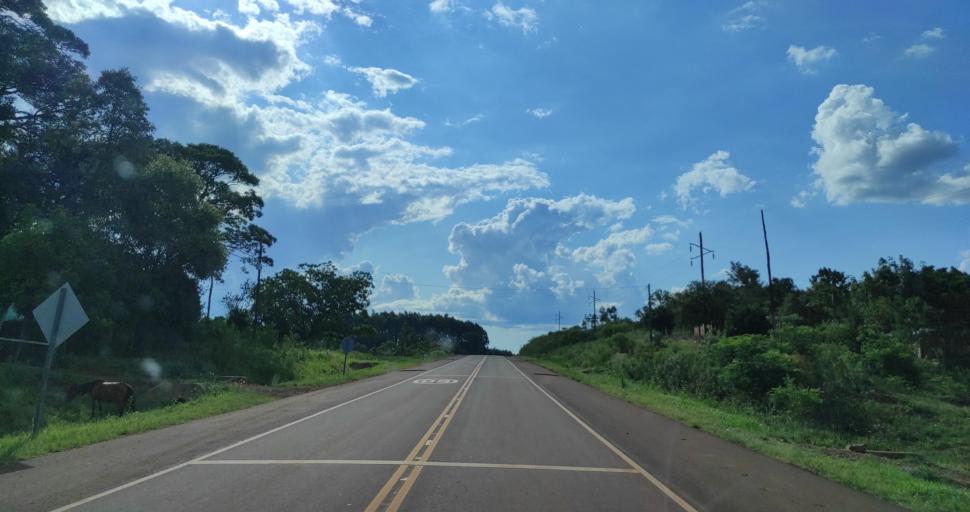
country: AR
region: Misiones
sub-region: Departamento de San Pedro
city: San Pedro
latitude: -26.3708
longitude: -53.9388
